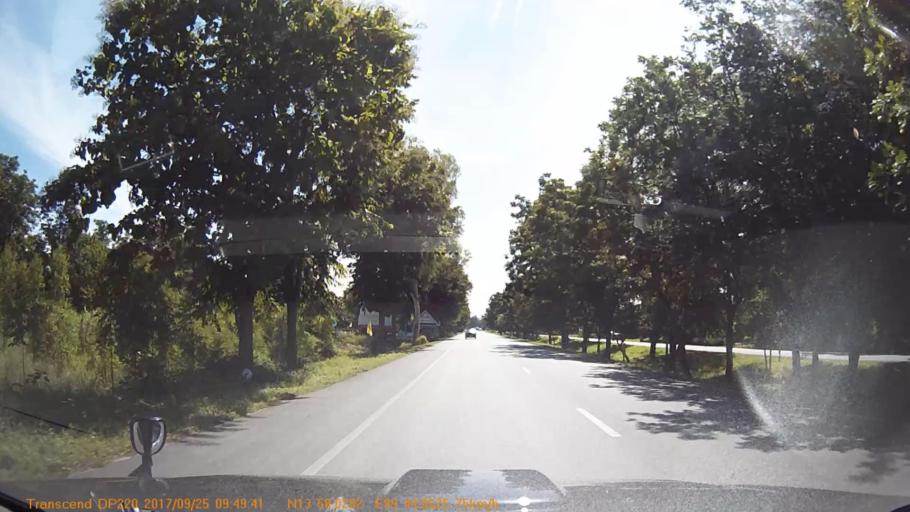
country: TH
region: Kanchanaburi
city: Tha Maka
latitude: 13.9671
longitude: 99.7347
